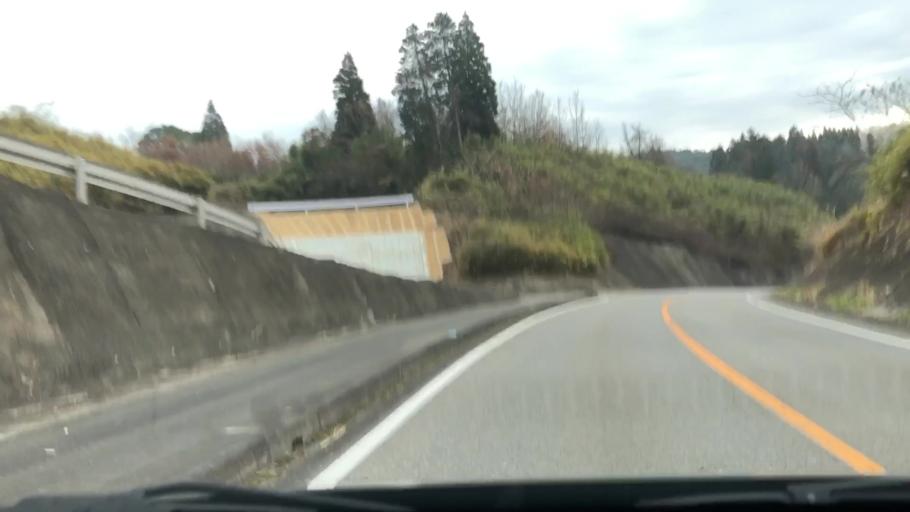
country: JP
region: Oita
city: Usuki
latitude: 33.0086
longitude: 131.6452
